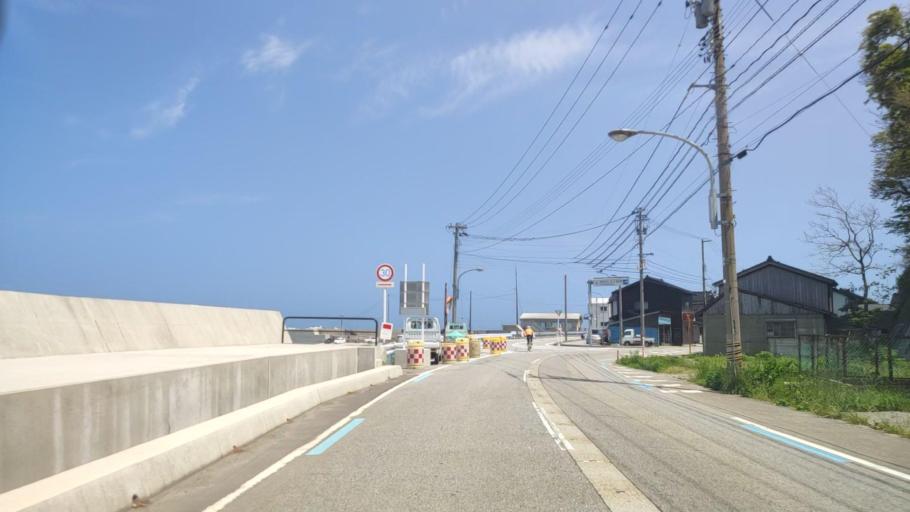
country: JP
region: Toyama
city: Nyuzen
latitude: 36.9722
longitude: 137.5861
